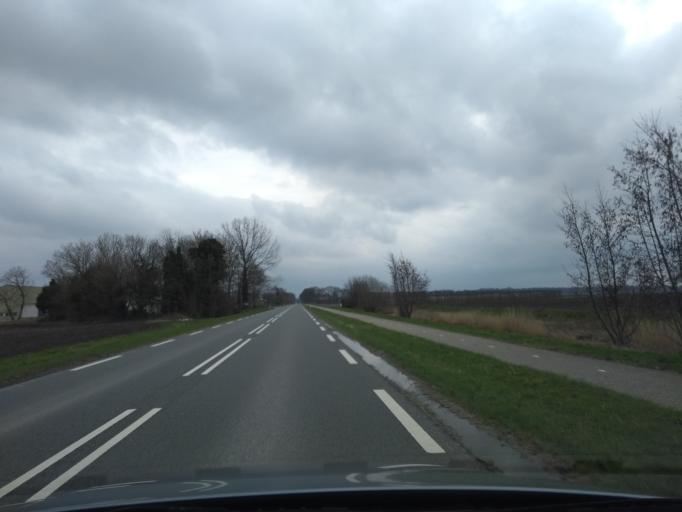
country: NL
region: Flevoland
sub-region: Gemeente Noordoostpolder
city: Ens
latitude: 52.7294
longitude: 5.8622
